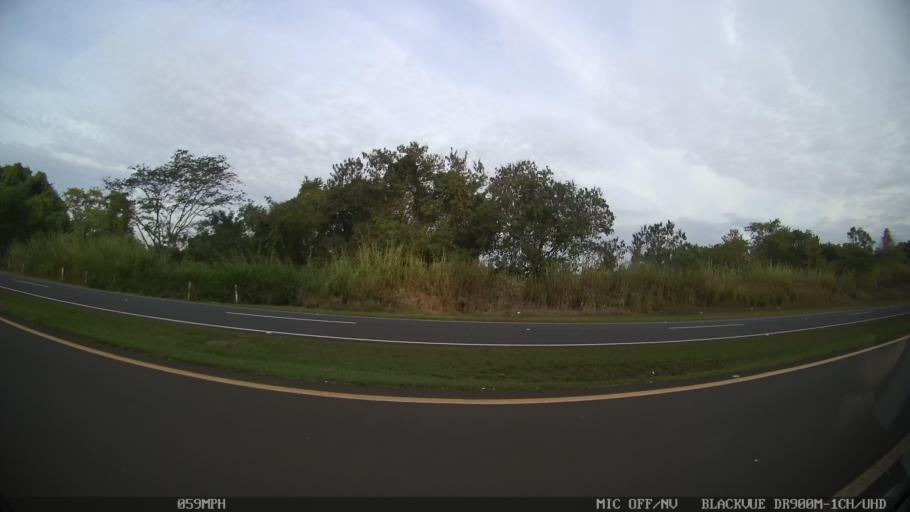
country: BR
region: Sao Paulo
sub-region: Piracicaba
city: Piracicaba
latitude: -22.6902
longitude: -47.5866
